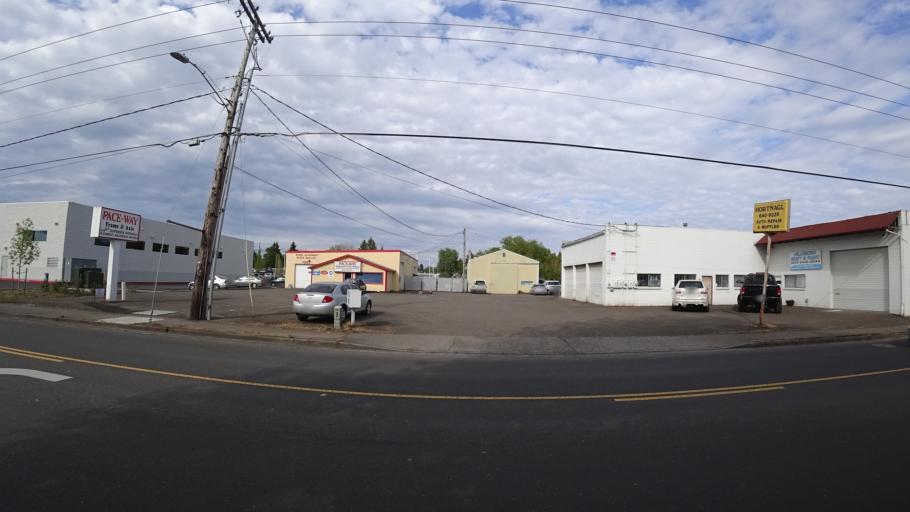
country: US
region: Oregon
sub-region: Washington County
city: Hillsboro
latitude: 45.5077
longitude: -122.9670
